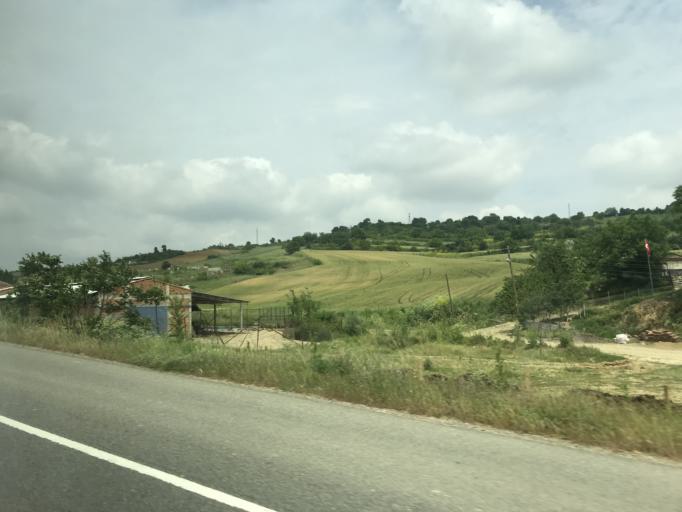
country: TR
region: Tekirdag
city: Inecik
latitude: 40.9384
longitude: 27.2787
